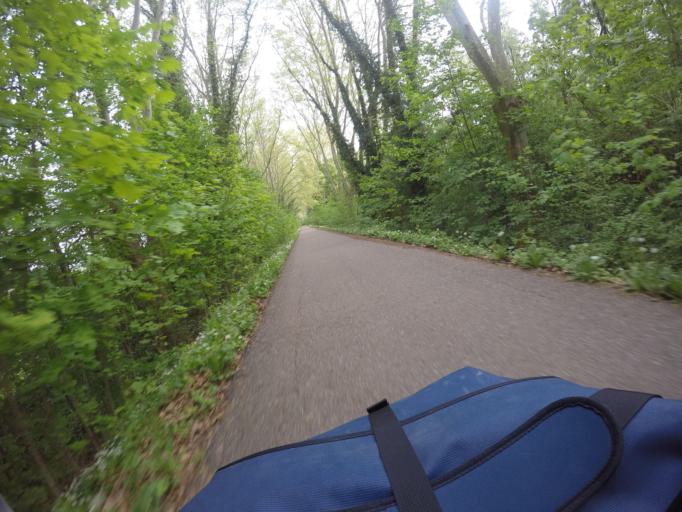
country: DE
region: Baden-Wuerttemberg
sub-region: Freiburg Region
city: Kehl
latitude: 48.6083
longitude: 7.8074
